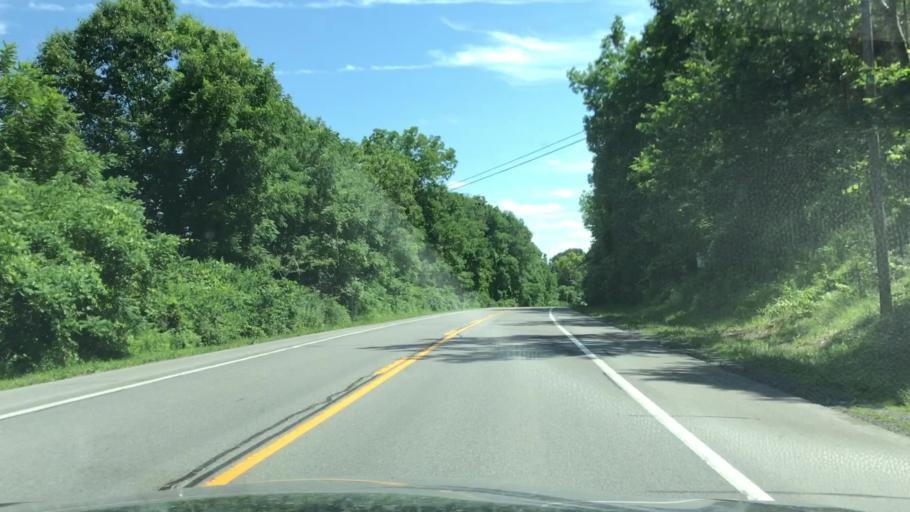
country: US
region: New York
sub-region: Livingston County
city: Mount Morris
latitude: 42.7517
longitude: -77.8835
